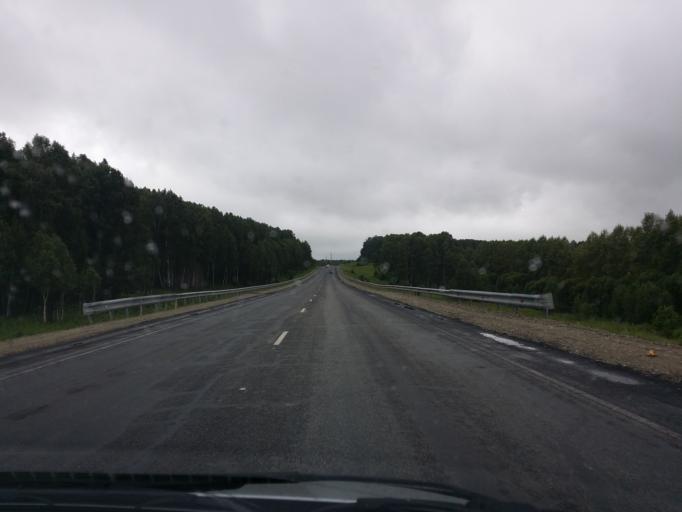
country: RU
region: Altai Krai
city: Troitskoye
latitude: 53.0804
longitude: 84.7037
